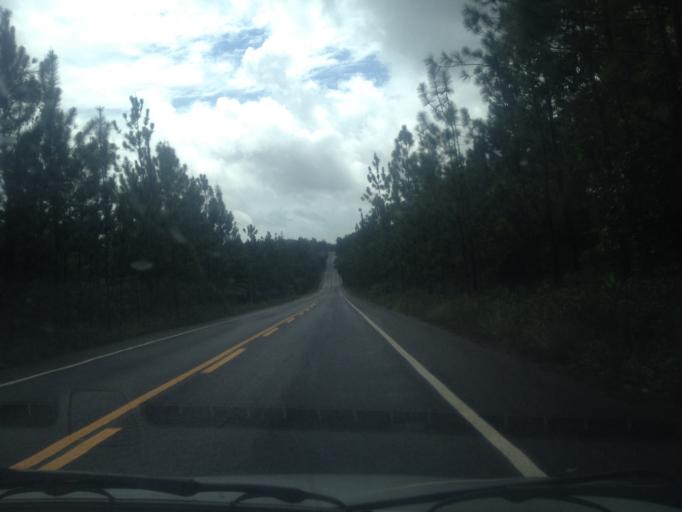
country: BR
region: Bahia
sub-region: Entre Rios
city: Entre Rios
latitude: -12.1118
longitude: -37.7856
